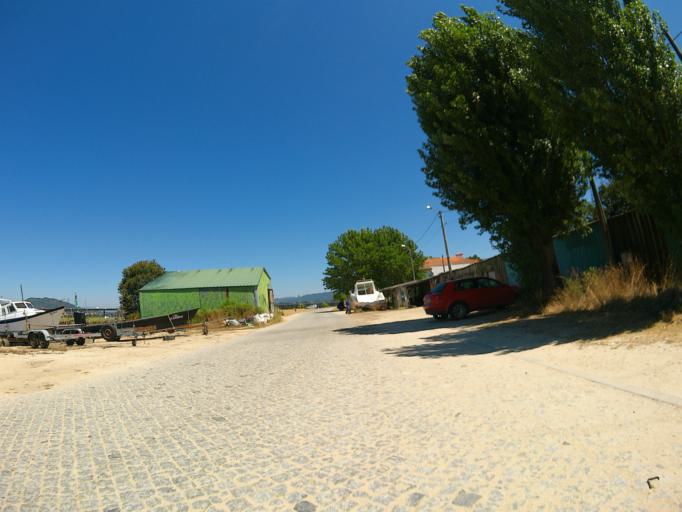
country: PT
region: Viana do Castelo
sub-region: Viana do Castelo
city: Meadela
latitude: 41.6883
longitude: -8.7922
